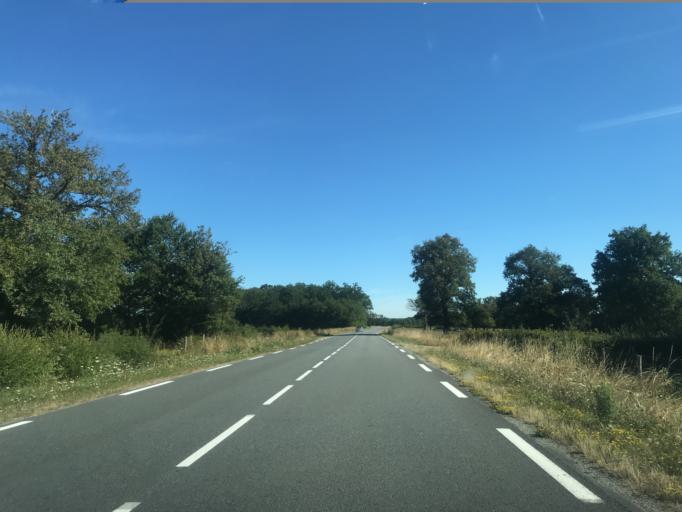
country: FR
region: Limousin
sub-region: Departement de la Creuse
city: Gouzon
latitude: 46.1717
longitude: 2.2222
